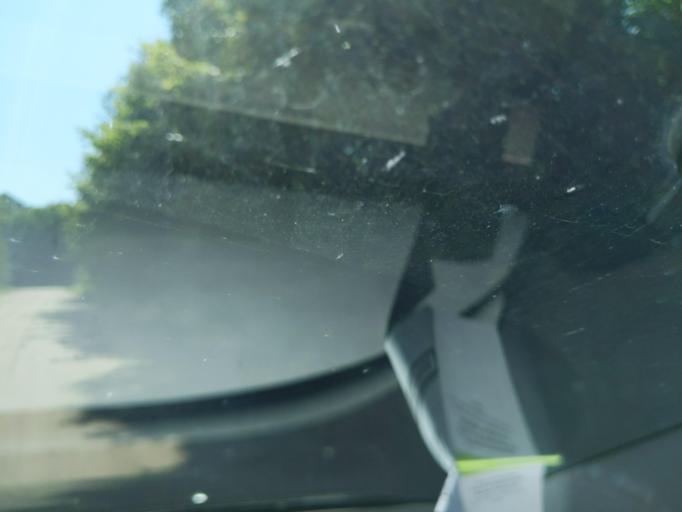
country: US
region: Michigan
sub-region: Cheboygan County
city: Cheboygan
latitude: 45.6790
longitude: -84.6523
